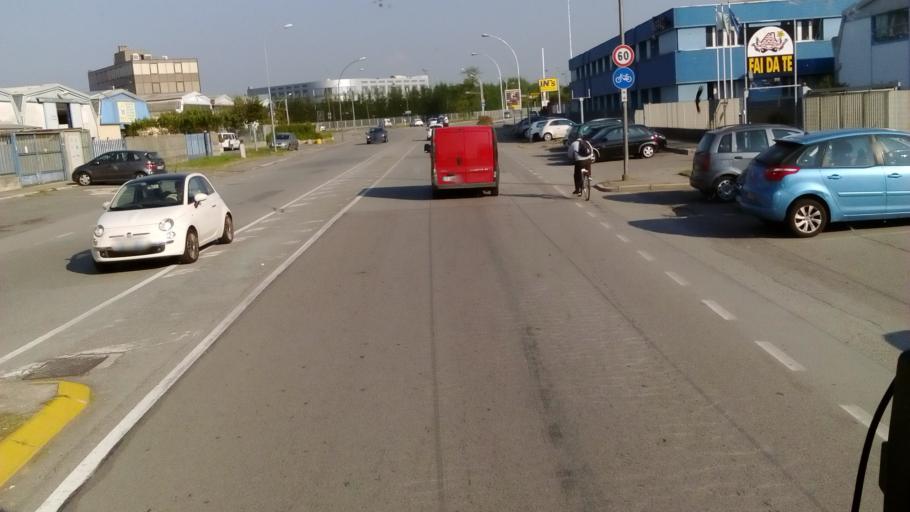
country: IT
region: Lombardy
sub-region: Provincia di Bergamo
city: Ciserano
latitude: 45.5920
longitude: 9.6059
